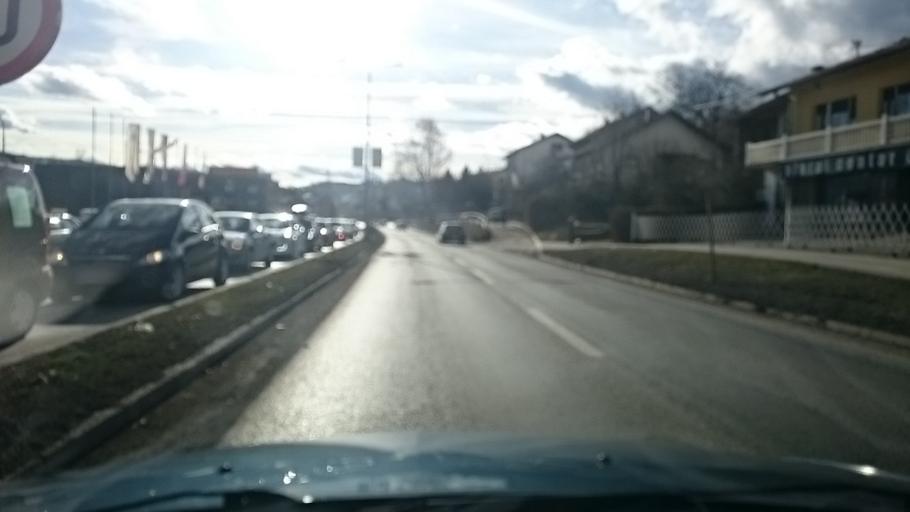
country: BA
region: Republika Srpska
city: Banja Luka
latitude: 44.7780
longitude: 17.1849
